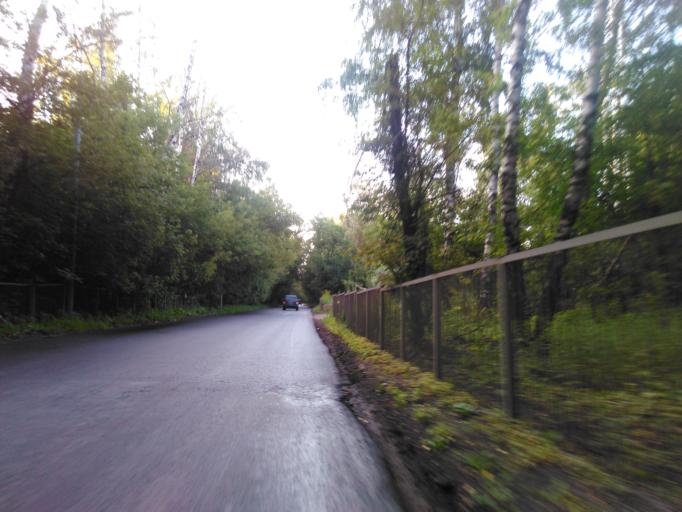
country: RU
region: Moskovskaya
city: Bogorodskoye
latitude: 55.8213
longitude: 37.6950
